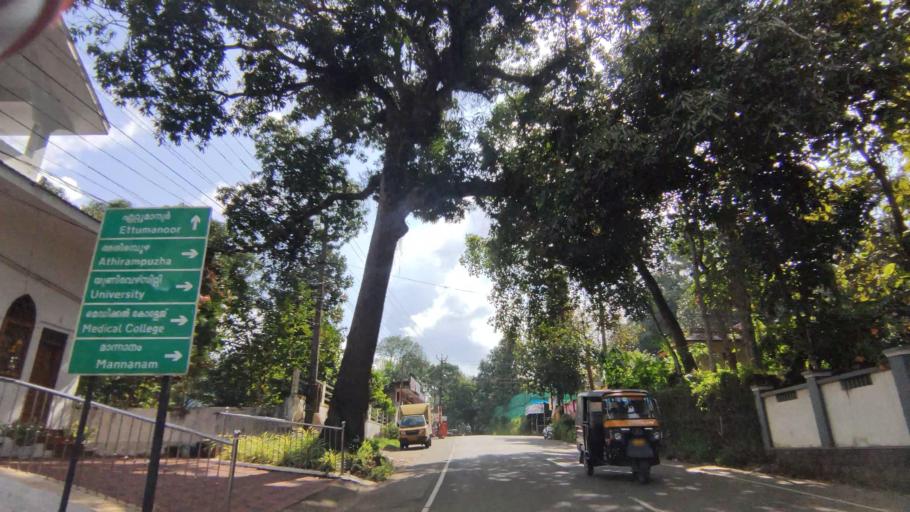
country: IN
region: Kerala
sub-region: Kottayam
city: Kottayam
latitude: 9.6740
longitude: 76.5321
